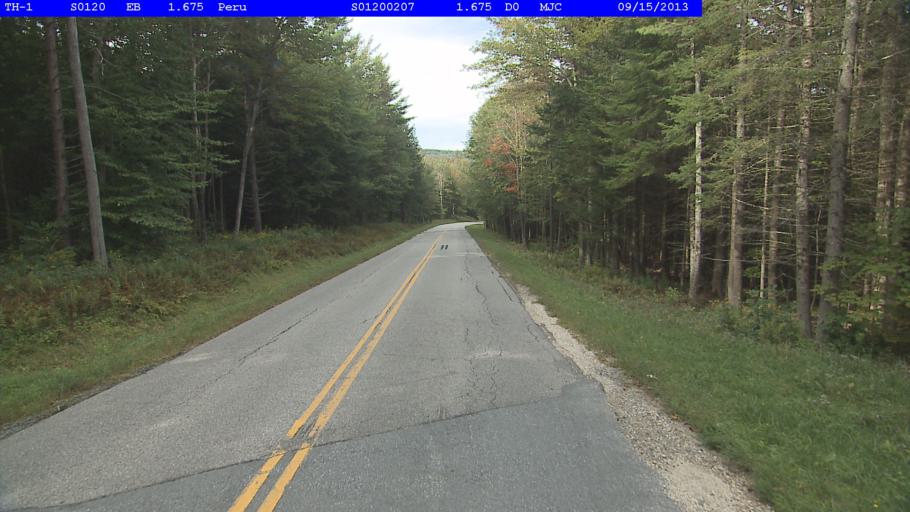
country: US
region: Vermont
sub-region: Bennington County
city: Manchester Center
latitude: 43.2486
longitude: -72.8908
